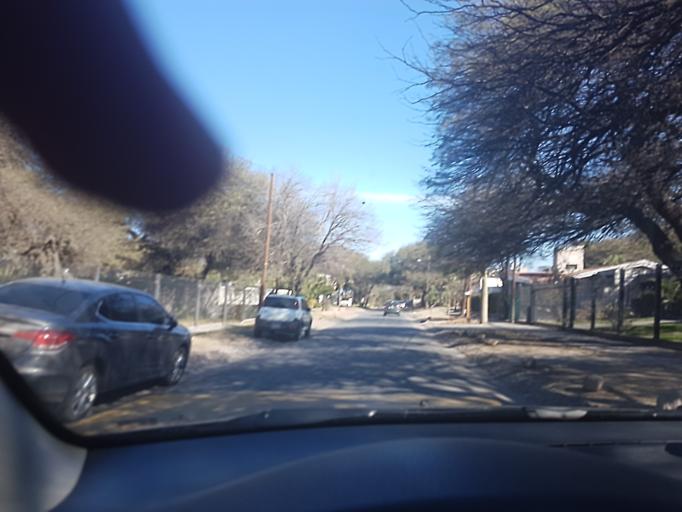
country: AR
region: Cordoba
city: Villa Allende
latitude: -31.3506
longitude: -64.2520
